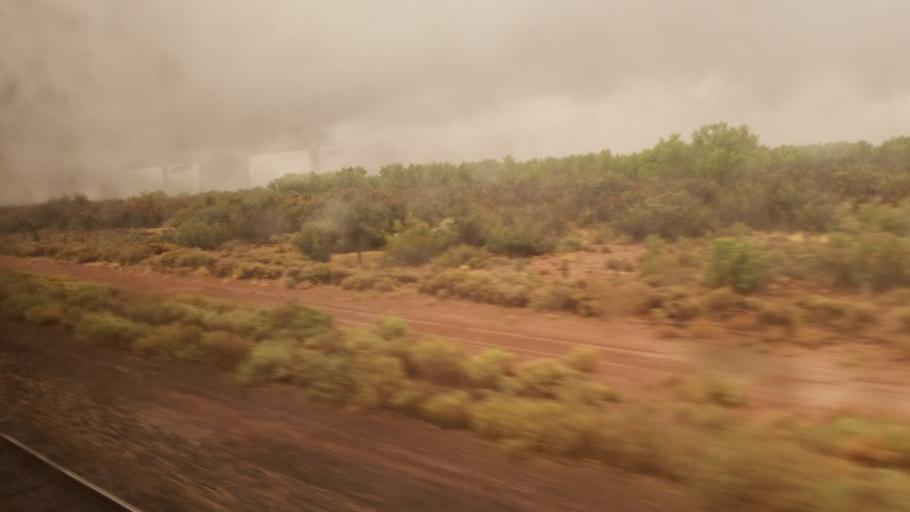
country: US
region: Arizona
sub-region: Navajo County
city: Holbrook
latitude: 34.9033
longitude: -110.2290
